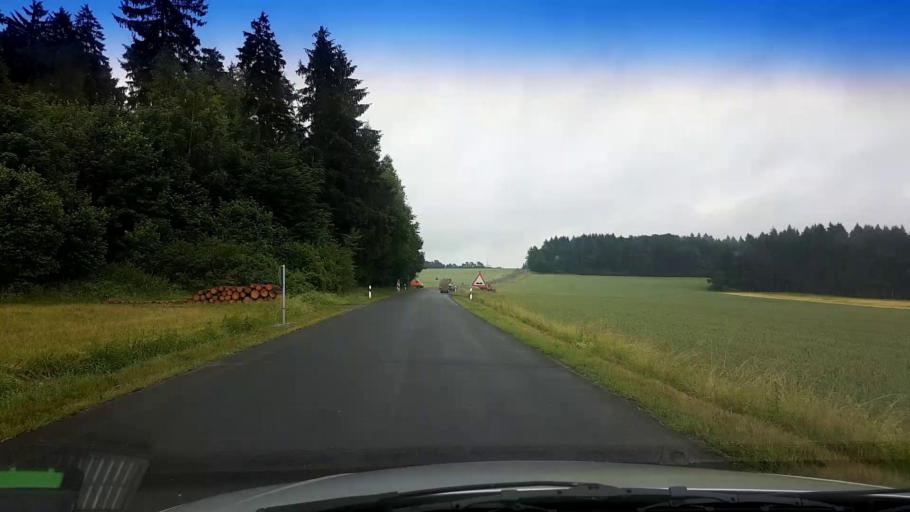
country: DE
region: Bavaria
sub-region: Upper Franconia
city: Wattendorf
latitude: 50.0555
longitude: 11.1194
